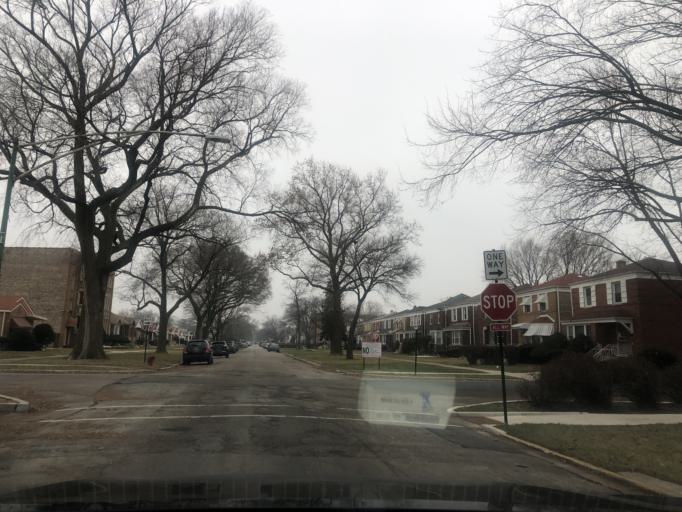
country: US
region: Illinois
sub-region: Cook County
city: Evergreen Park
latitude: 41.7422
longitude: -87.6228
